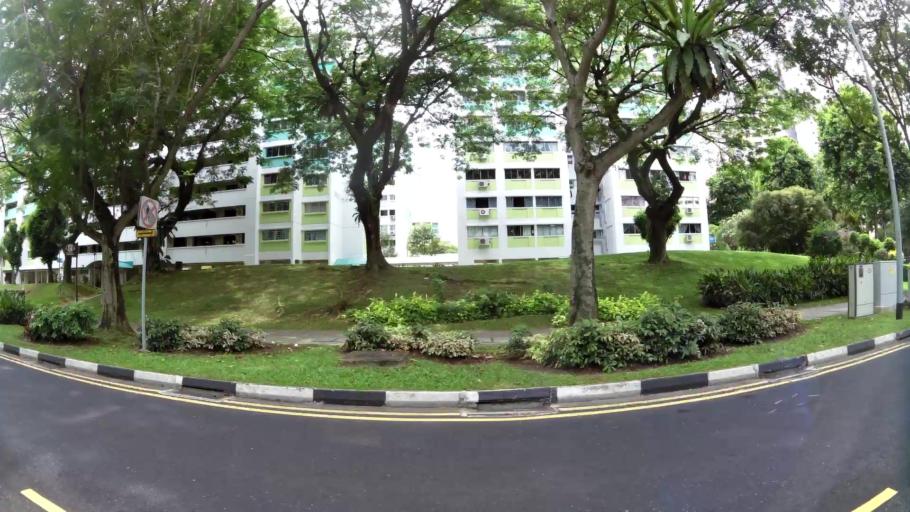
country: MY
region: Johor
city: Johor Bahru
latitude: 1.3797
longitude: 103.7680
